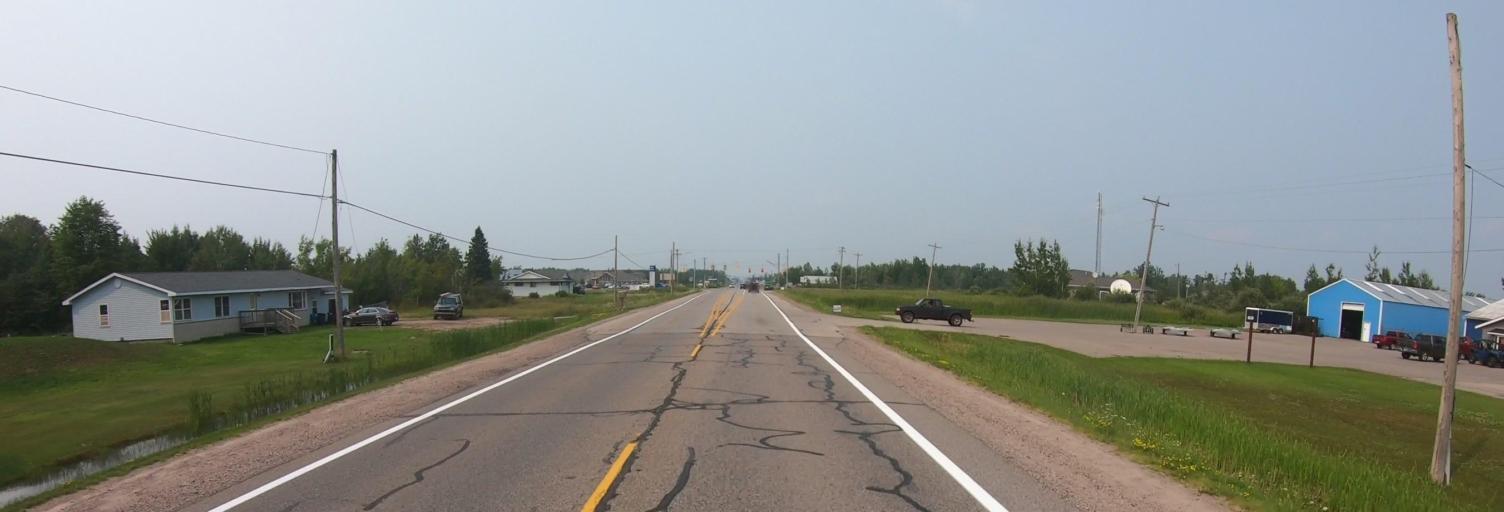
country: US
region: Michigan
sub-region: Chippewa County
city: Sault Ste. Marie
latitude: 46.4610
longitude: -84.3541
